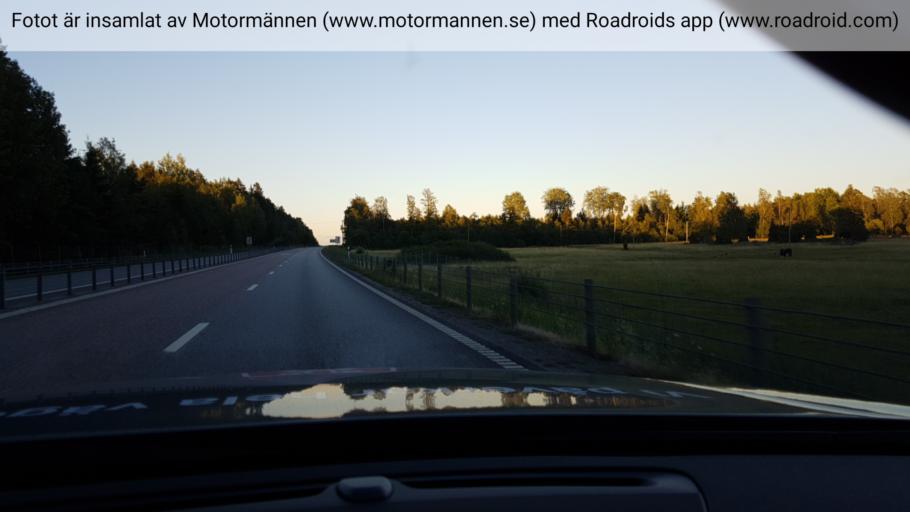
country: SE
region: Vaestmanland
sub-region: Hallstahammars Kommun
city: Hallstahammar
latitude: 59.5826
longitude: 16.1639
